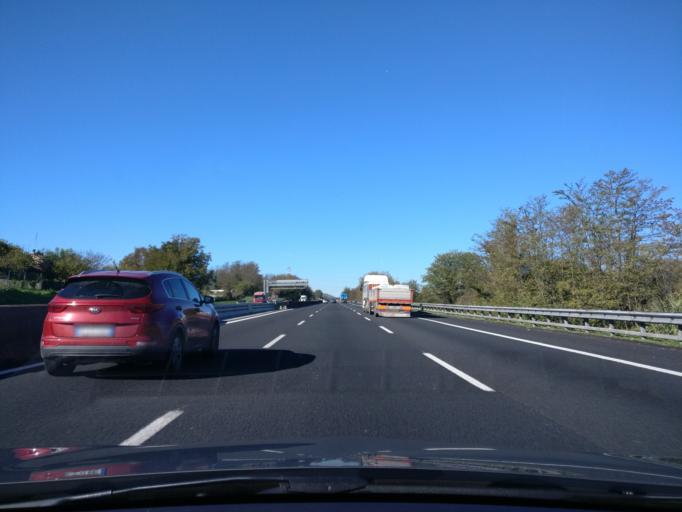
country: IT
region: Latium
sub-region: Citta metropolitana di Roma Capitale
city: Valmontone
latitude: 41.7727
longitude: 12.8952
